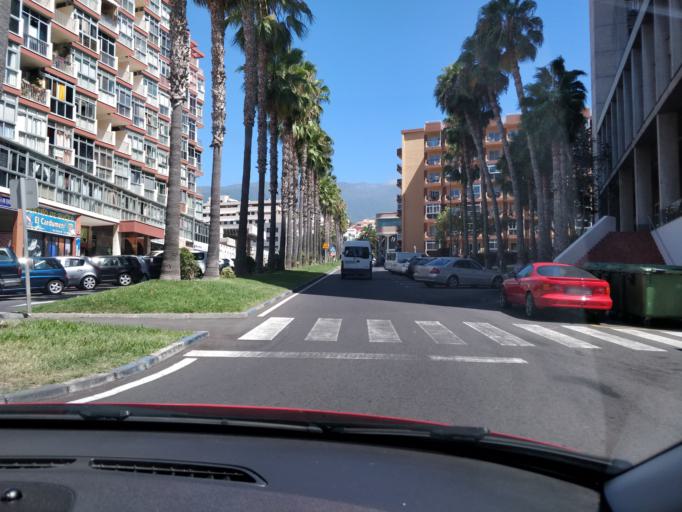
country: ES
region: Canary Islands
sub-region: Provincia de Santa Cruz de Tenerife
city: Puerto de la Cruz
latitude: 28.4135
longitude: -16.5560
